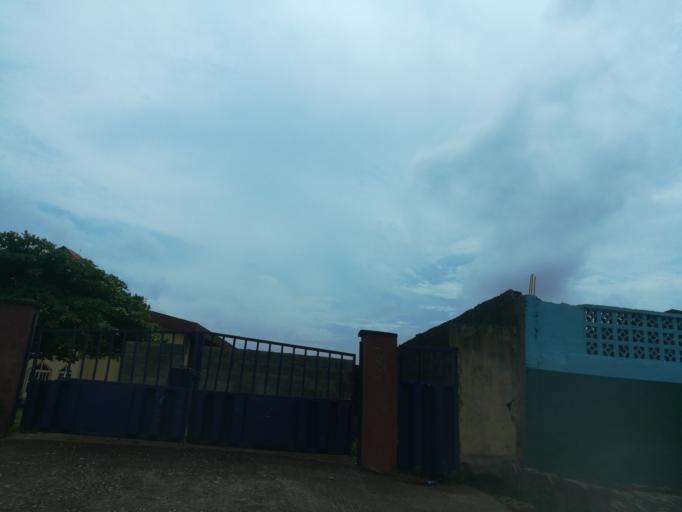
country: NG
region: Lagos
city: Ojota
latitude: 6.5712
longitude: 3.3610
